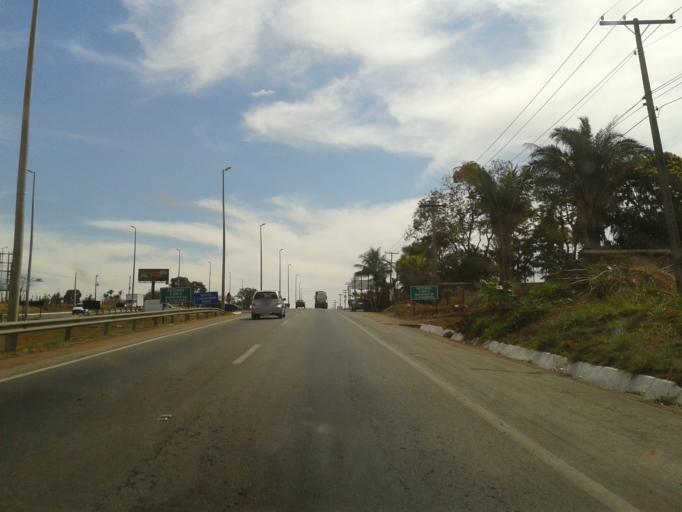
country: BR
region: Goias
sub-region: Goiania
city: Goiania
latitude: -16.6298
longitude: -49.3503
